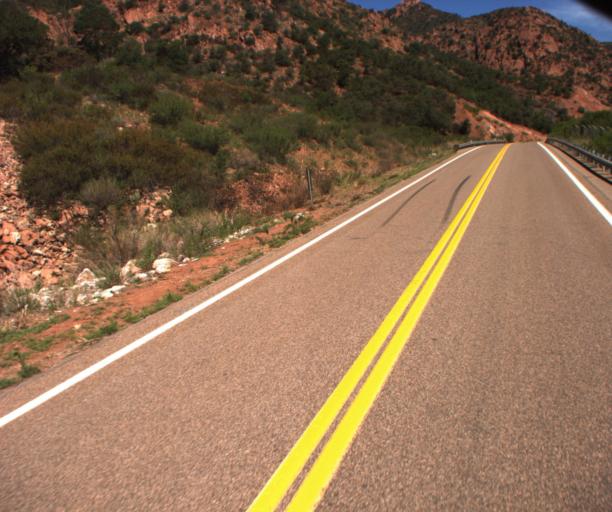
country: US
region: Arizona
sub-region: Greenlee County
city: Morenci
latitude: 33.1473
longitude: -109.3749
